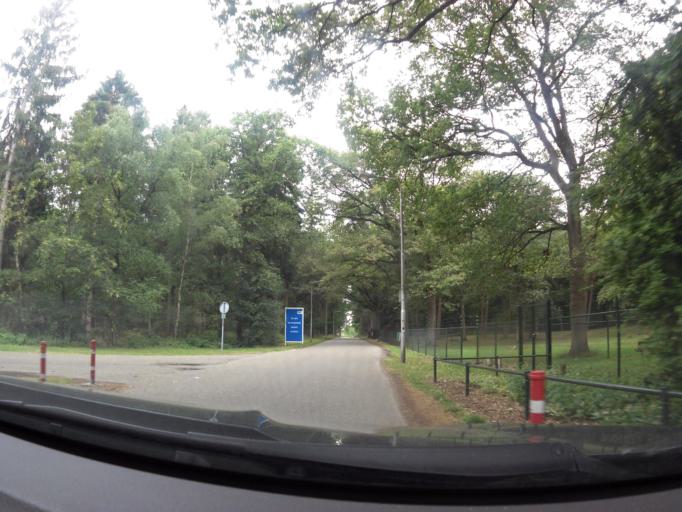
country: NL
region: Limburg
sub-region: Gemeente Venlo
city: Arcen
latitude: 51.4965
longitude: 6.1820
